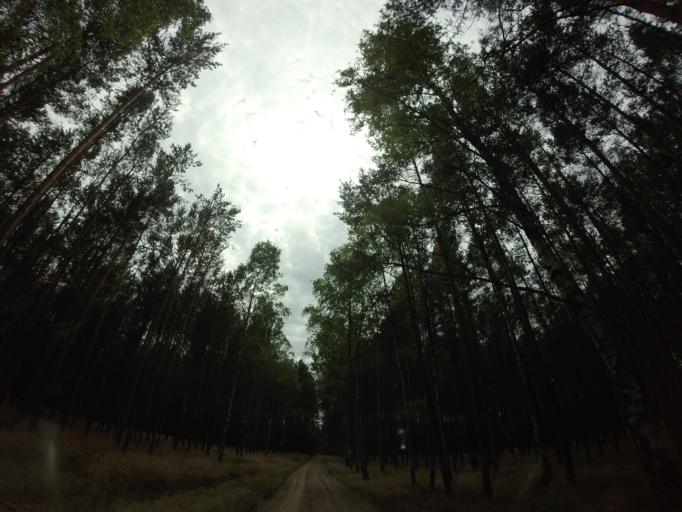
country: PL
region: West Pomeranian Voivodeship
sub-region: Powiat choszczenski
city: Drawno
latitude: 53.1663
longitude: 15.7872
